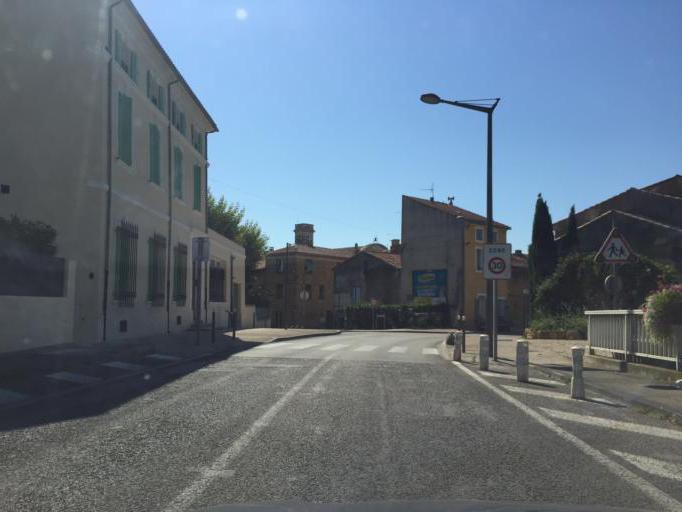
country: FR
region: Provence-Alpes-Cote d'Azur
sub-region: Departement du Vaucluse
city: Sorgues
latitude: 44.0136
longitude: 4.8718
